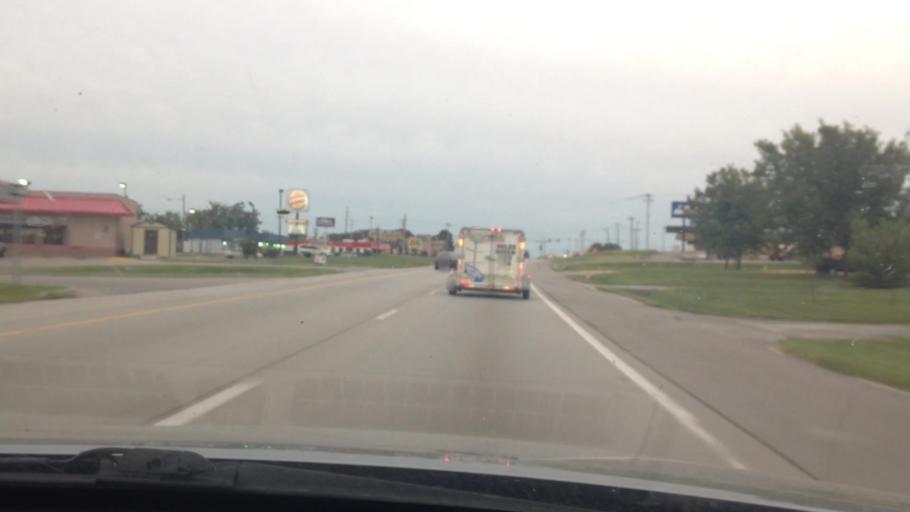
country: US
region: Missouri
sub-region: Jackson County
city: Raytown
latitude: 38.9889
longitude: -94.4667
